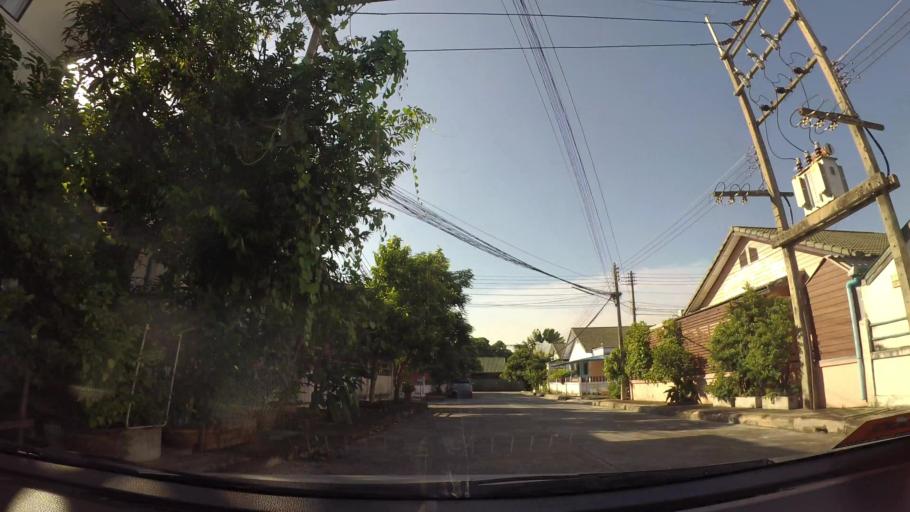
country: TH
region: Chon Buri
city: Si Racha
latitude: 13.1481
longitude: 100.9403
